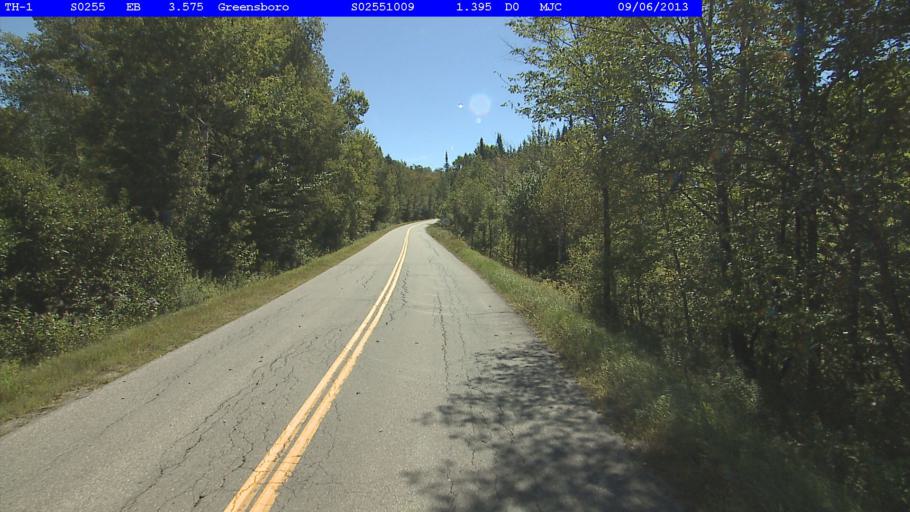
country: US
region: Vermont
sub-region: Caledonia County
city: Hardwick
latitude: 44.6210
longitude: -72.3287
